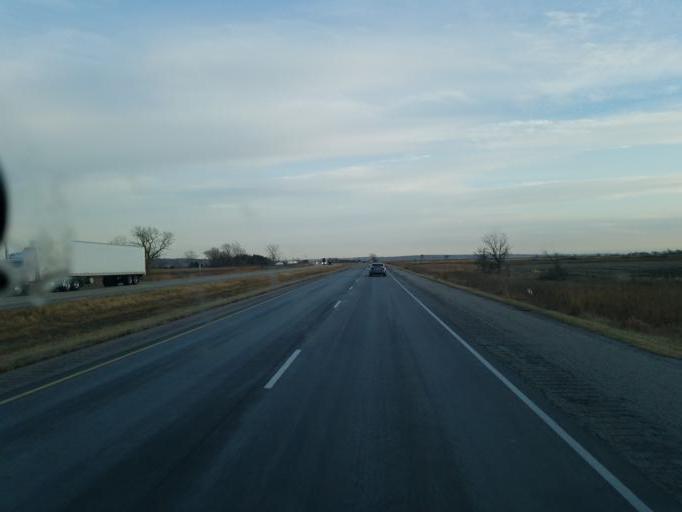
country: US
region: Iowa
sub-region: Harrison County
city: Missouri Valley
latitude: 41.5883
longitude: -95.9489
